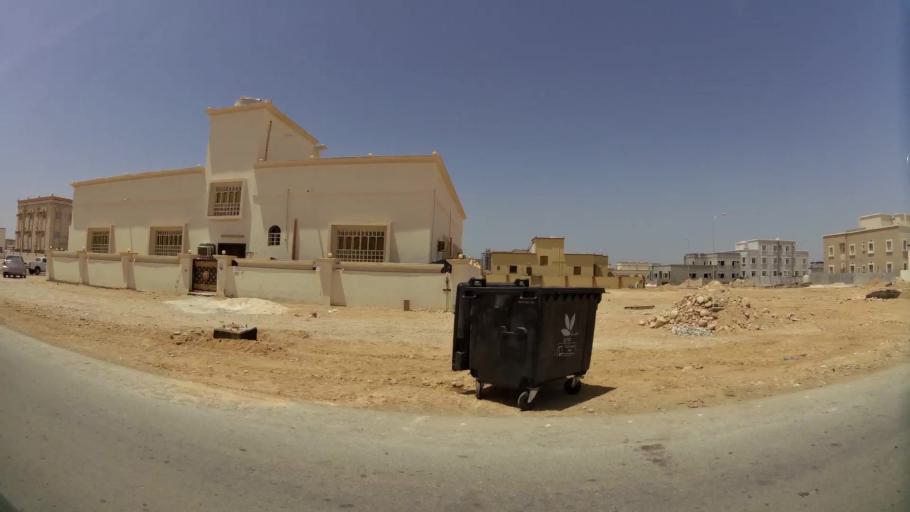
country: OM
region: Zufar
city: Salalah
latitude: 17.0737
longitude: 54.1951
